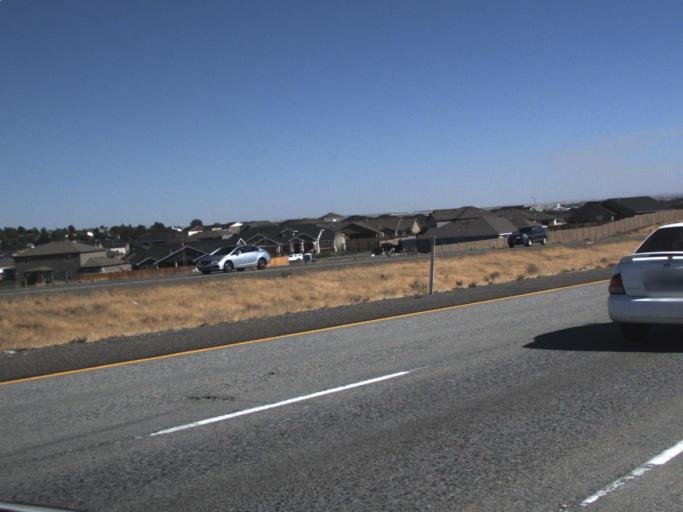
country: US
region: Washington
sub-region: Franklin County
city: West Pasco
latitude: 46.2587
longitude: -119.1604
